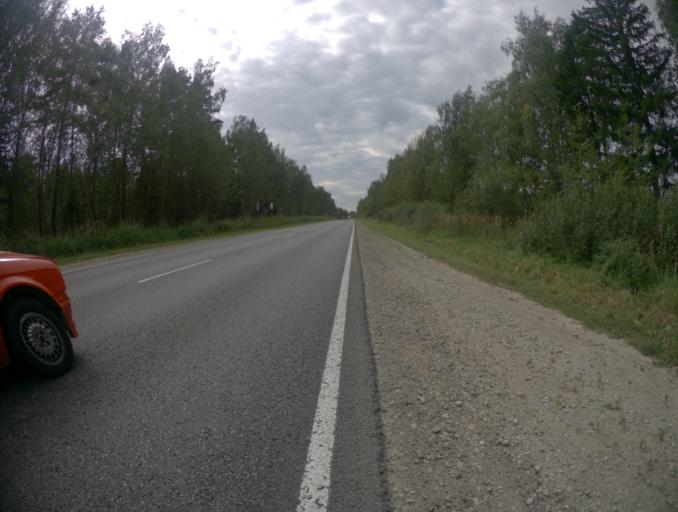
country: RU
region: Vladimir
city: Golovino
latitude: 56.0031
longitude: 40.5670
